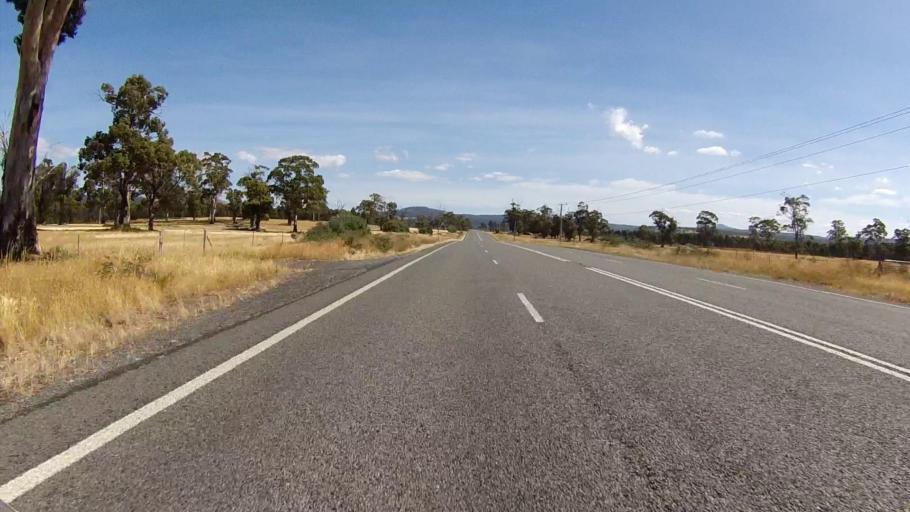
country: AU
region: Tasmania
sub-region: Sorell
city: Sorell
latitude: -42.5973
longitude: 147.7678
